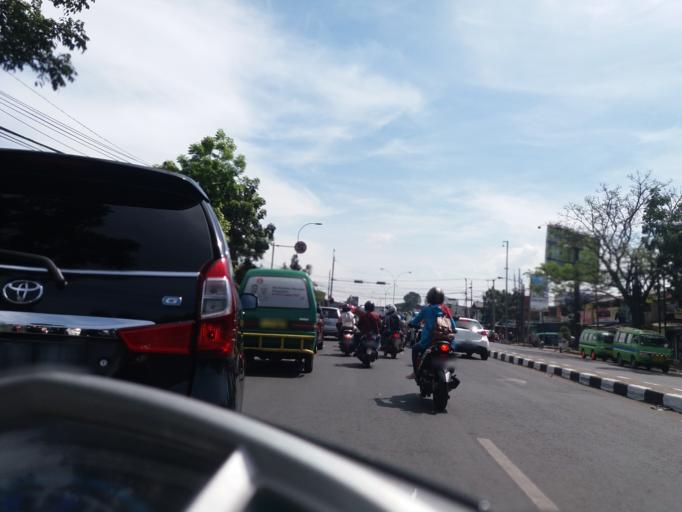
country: ID
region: West Java
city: Margahayukencana
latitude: -6.9459
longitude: 107.5904
